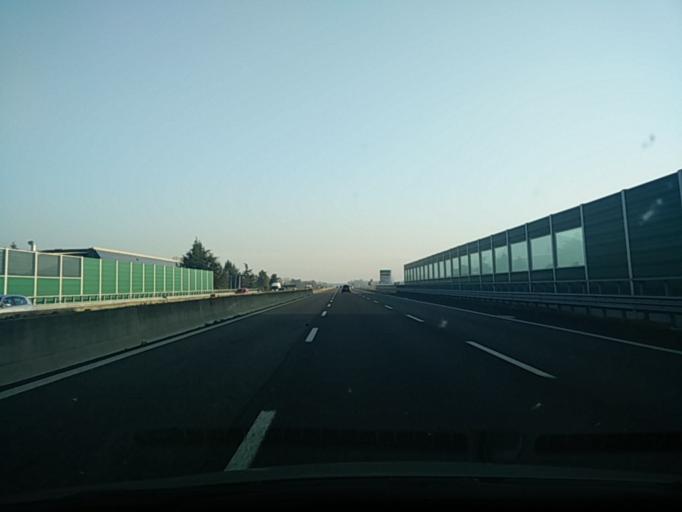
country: IT
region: Lombardy
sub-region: Provincia di Brescia
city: Capriolo
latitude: 45.6141
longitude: 9.9303
